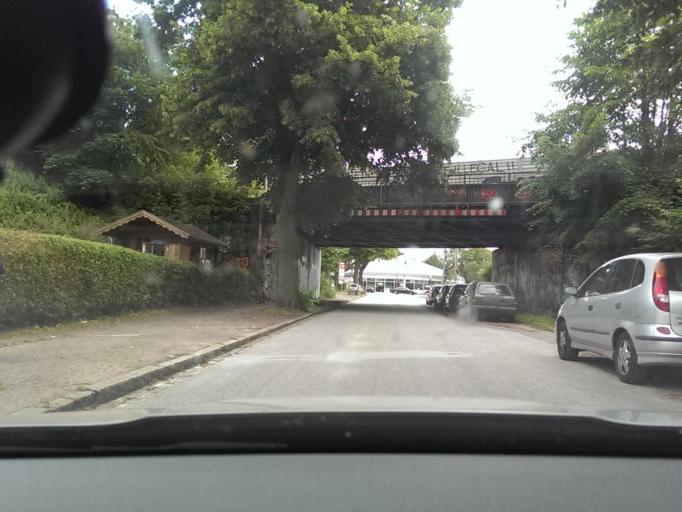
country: DE
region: Hamburg
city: Hamburg-Nord
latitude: 53.6047
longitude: 9.9664
